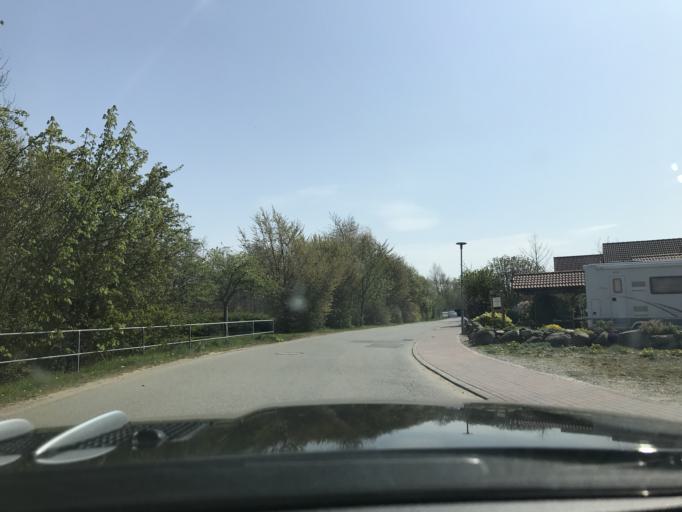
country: DE
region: Schleswig-Holstein
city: Grossenbrode
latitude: 54.3667
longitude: 11.0885
